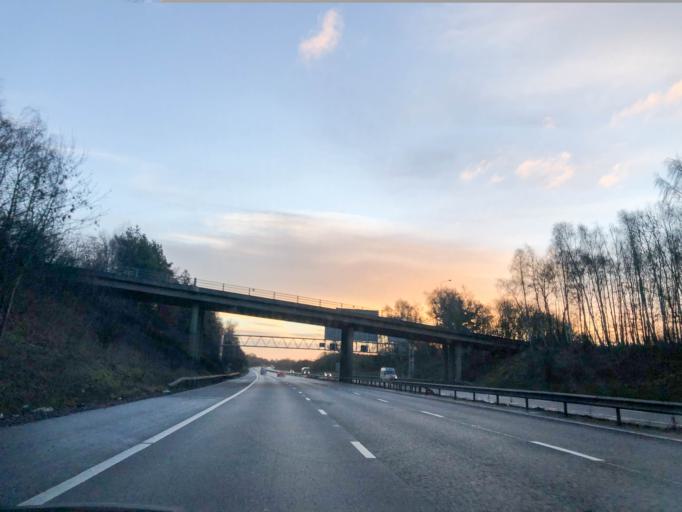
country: GB
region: England
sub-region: Warwickshire
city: Henley in Arden
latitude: 52.3351
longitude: -1.7741
